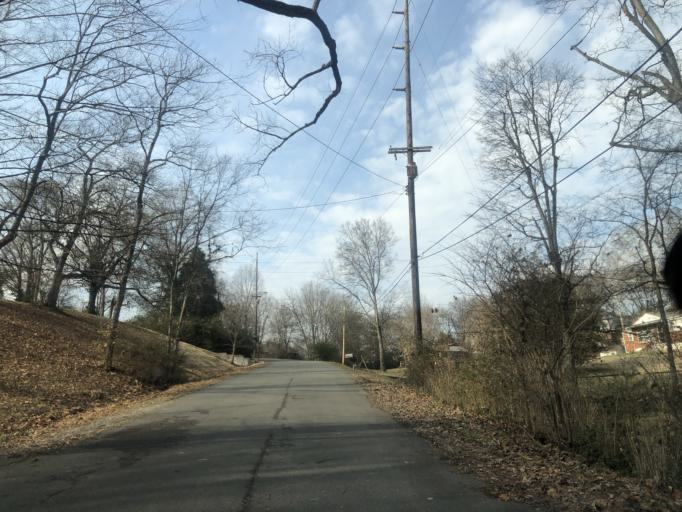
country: US
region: Tennessee
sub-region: Davidson County
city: Oak Hill
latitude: 36.1002
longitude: -86.7017
